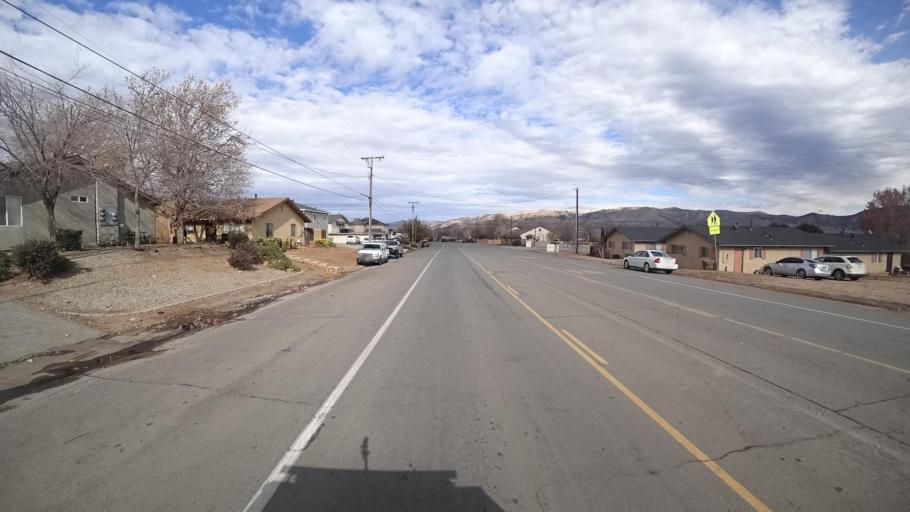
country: US
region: California
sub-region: Kern County
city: Golden Hills
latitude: 35.1271
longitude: -118.4859
